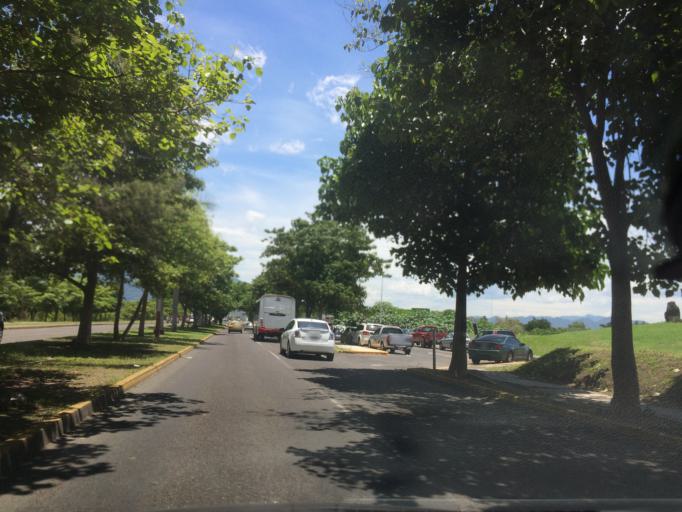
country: MX
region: Nayarit
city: Tepic
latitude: 21.4902
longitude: -104.8590
